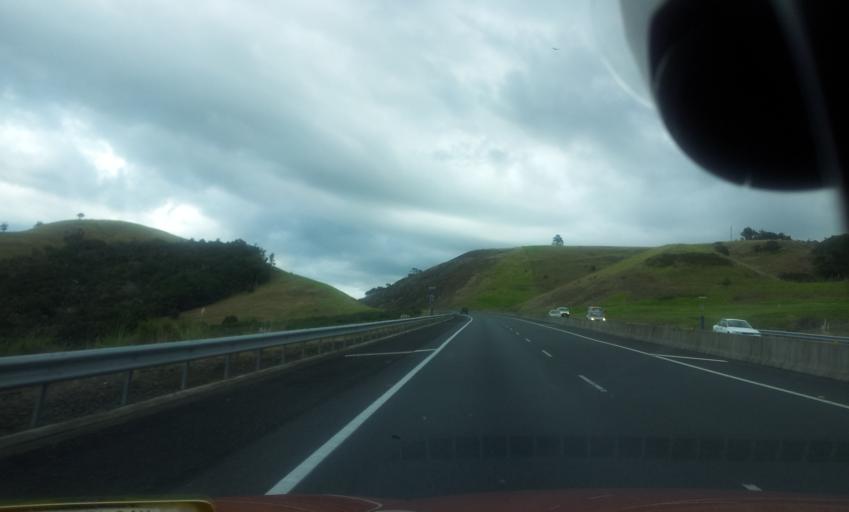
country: NZ
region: Auckland
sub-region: Auckland
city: Warkworth
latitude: -36.5478
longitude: 174.6806
